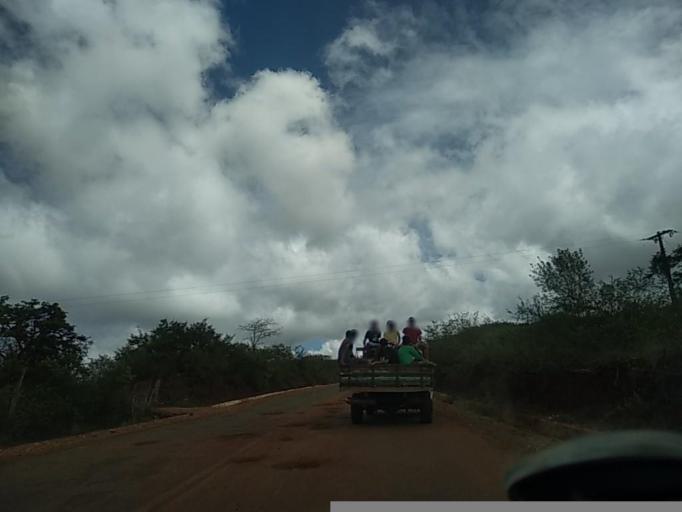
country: BR
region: Bahia
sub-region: Caetite
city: Caetite
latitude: -14.0281
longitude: -42.4881
